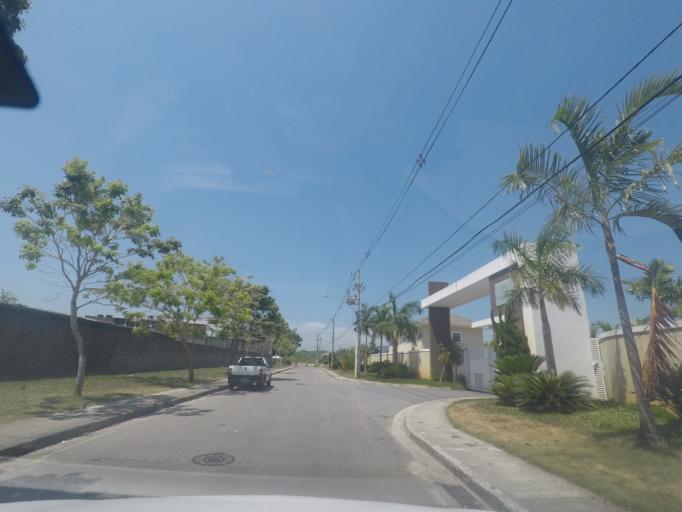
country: BR
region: Rio de Janeiro
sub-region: Nilopolis
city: Nilopolis
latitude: -22.9880
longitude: -43.4611
